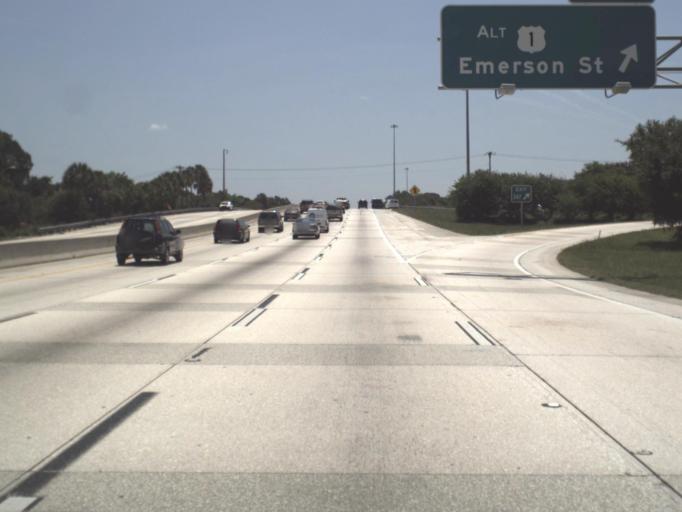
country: US
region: Florida
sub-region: Duval County
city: Jacksonville
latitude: 30.2922
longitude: -81.6316
